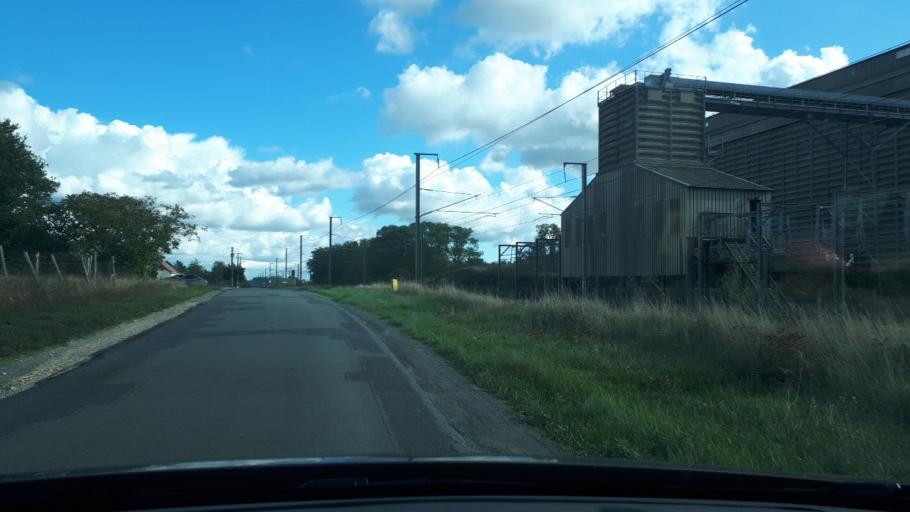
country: FR
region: Centre
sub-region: Departement du Loir-et-Cher
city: Saint-Aignan
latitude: 47.2952
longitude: 1.3658
